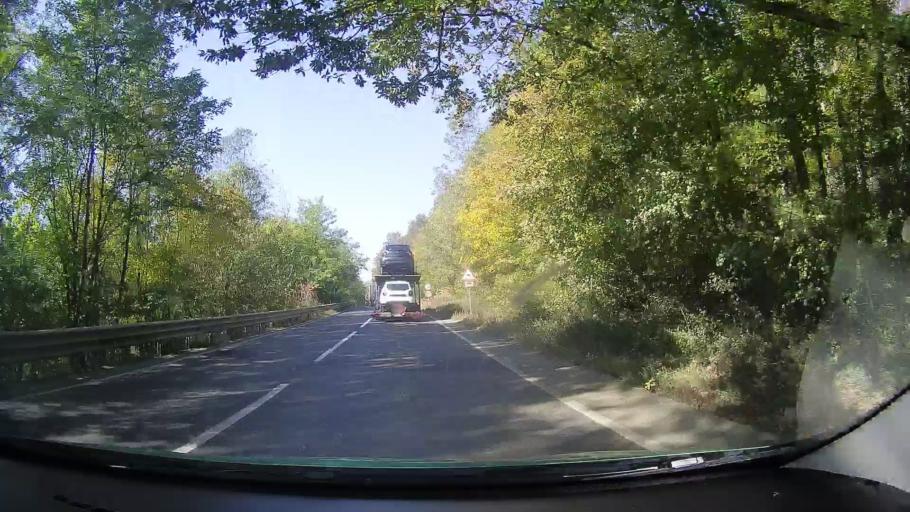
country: RO
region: Arad
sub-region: Comuna Bata
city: Bata
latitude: 46.0737
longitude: 22.0353
